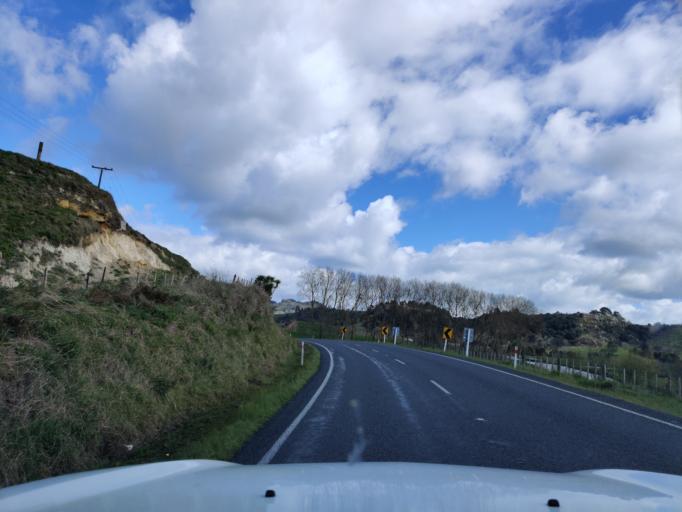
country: NZ
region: Waikato
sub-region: Waikato District
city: Ngaruawahia
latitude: -37.5798
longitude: 175.2216
